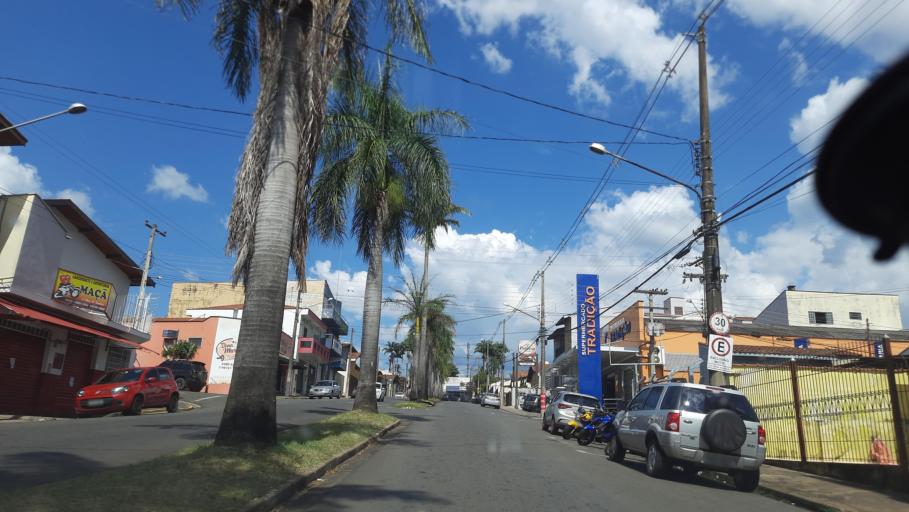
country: BR
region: Sao Paulo
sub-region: Sao Jose Do Rio Pardo
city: Sao Jose do Rio Pardo
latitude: -21.6032
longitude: -46.8999
